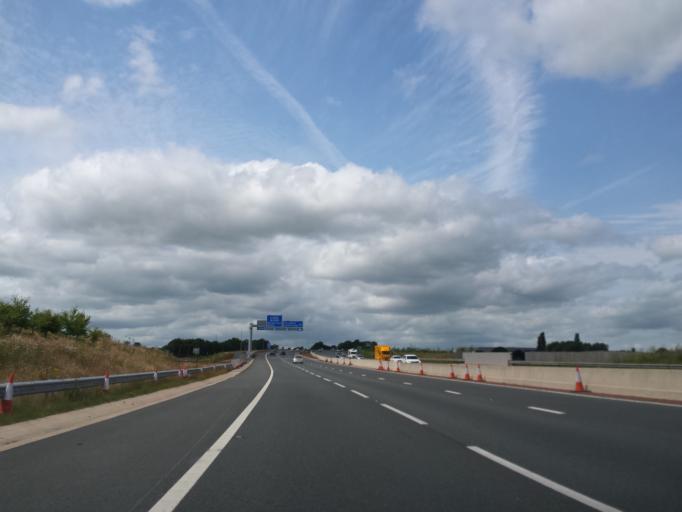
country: GB
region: England
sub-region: North Yorkshire
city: Bedale
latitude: 54.2971
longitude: -1.5591
